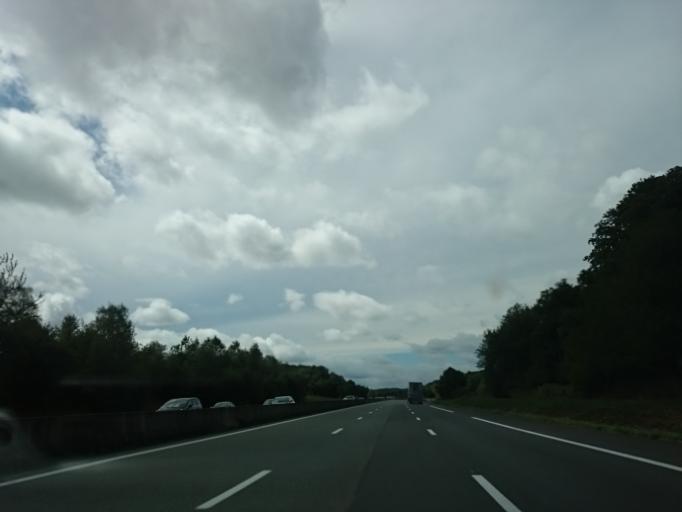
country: FR
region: Centre
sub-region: Departement d'Eure-et-Loir
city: Authon-du-Perche
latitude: 48.2163
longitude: 0.9509
